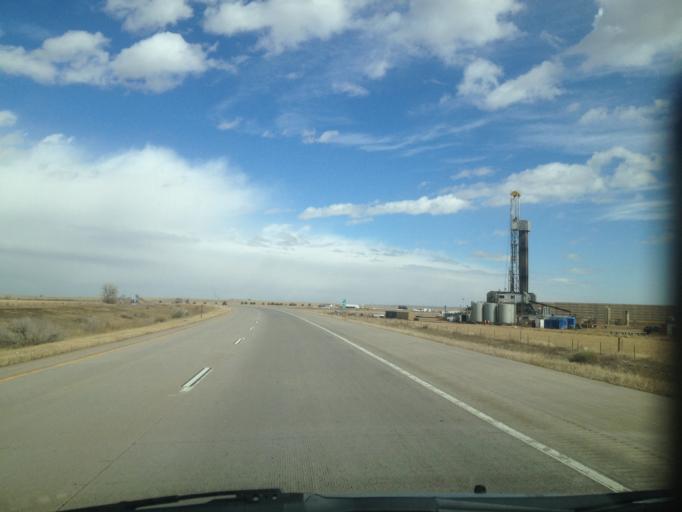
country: US
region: Colorado
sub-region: Weld County
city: Keenesburg
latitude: 40.1202
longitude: -104.5038
